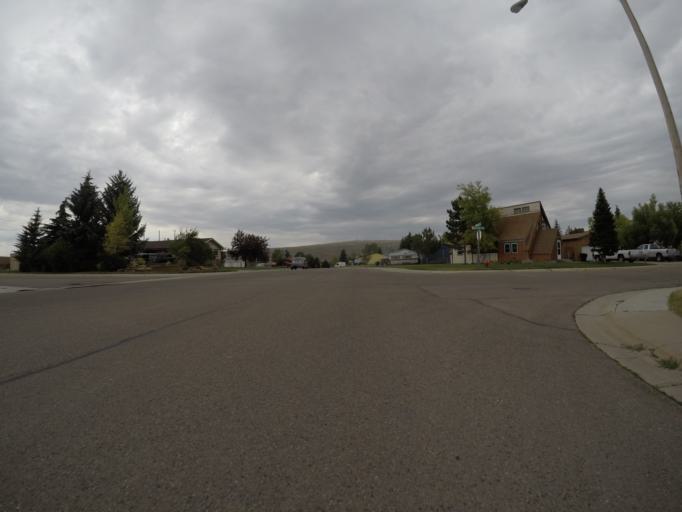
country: US
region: Wyoming
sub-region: Lincoln County
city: Kemmerer
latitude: 41.7903
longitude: -110.5497
